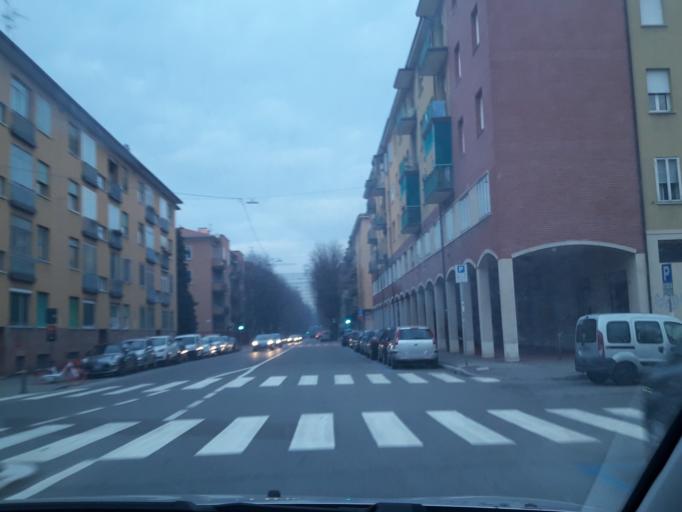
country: IT
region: Emilia-Romagna
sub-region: Provincia di Bologna
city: Bologna
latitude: 44.4998
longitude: 11.3105
